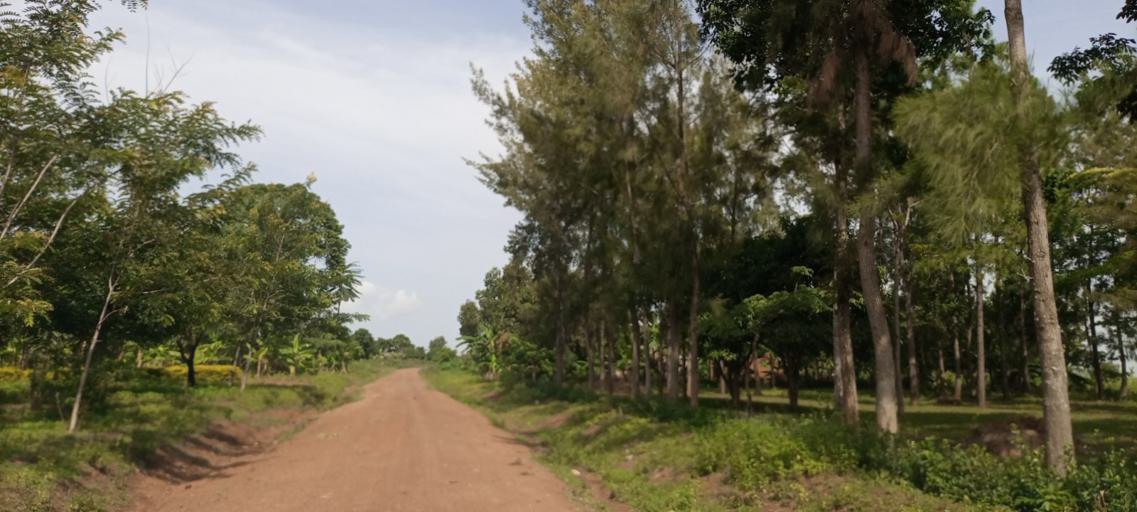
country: UG
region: Eastern Region
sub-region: Mbale District
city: Mbale
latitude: 1.1343
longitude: 34.0544
